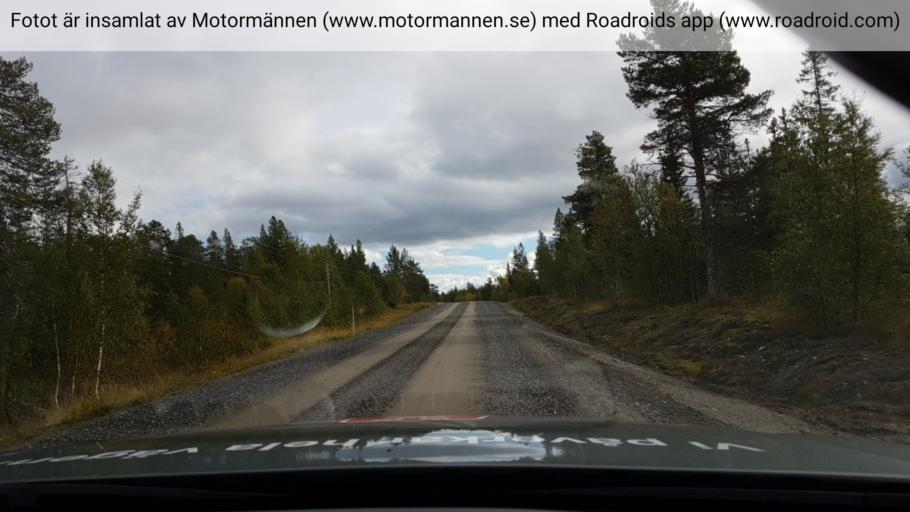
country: NO
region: Nord-Trondelag
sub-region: Snasa
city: Snaase
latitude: 63.7346
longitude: 12.5074
